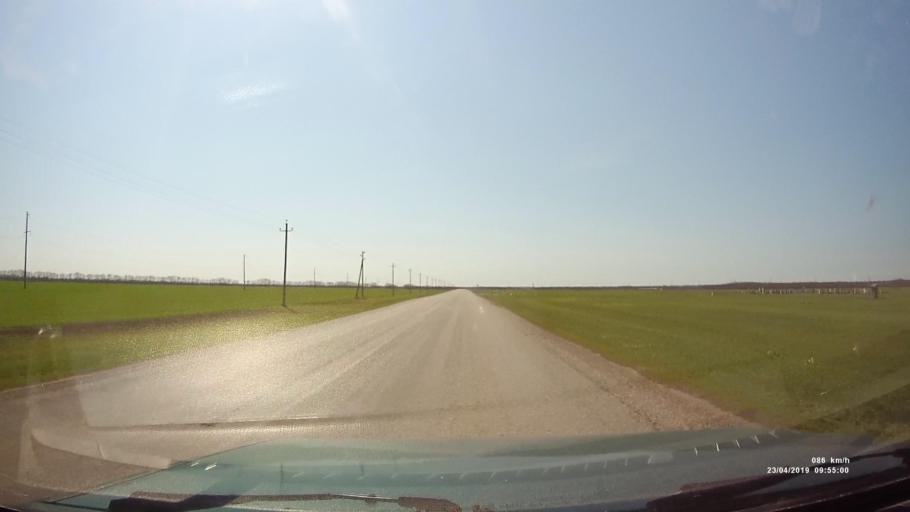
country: RU
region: Rostov
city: Orlovskiy
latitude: 46.8144
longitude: 42.0593
